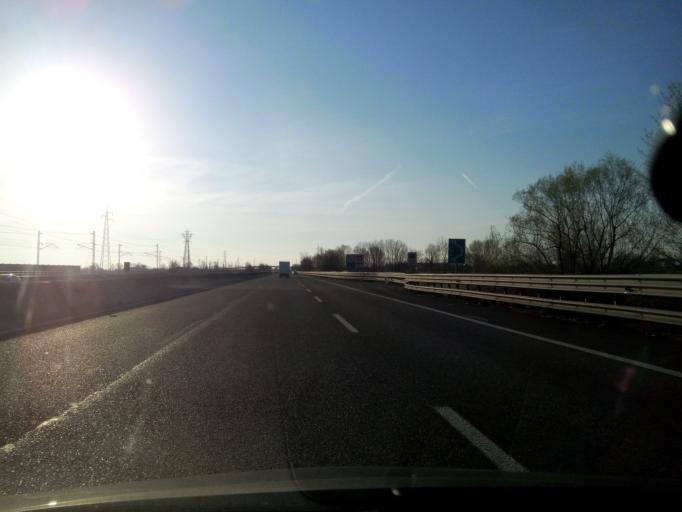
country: IT
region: Emilia-Romagna
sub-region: Provincia di Piacenza
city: Pontenure
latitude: 45.0040
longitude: 9.8044
